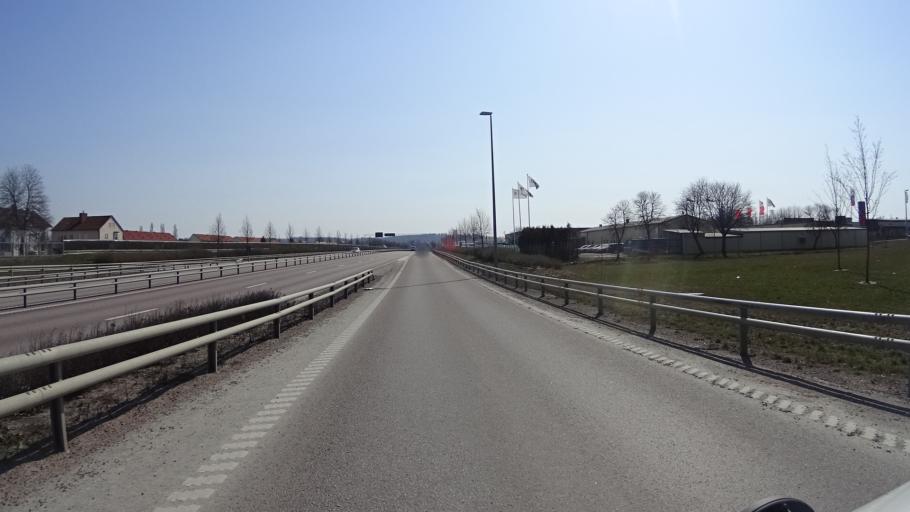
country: SE
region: OEstergoetland
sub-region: Motala Kommun
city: Motala
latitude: 58.5441
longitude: 15.0151
